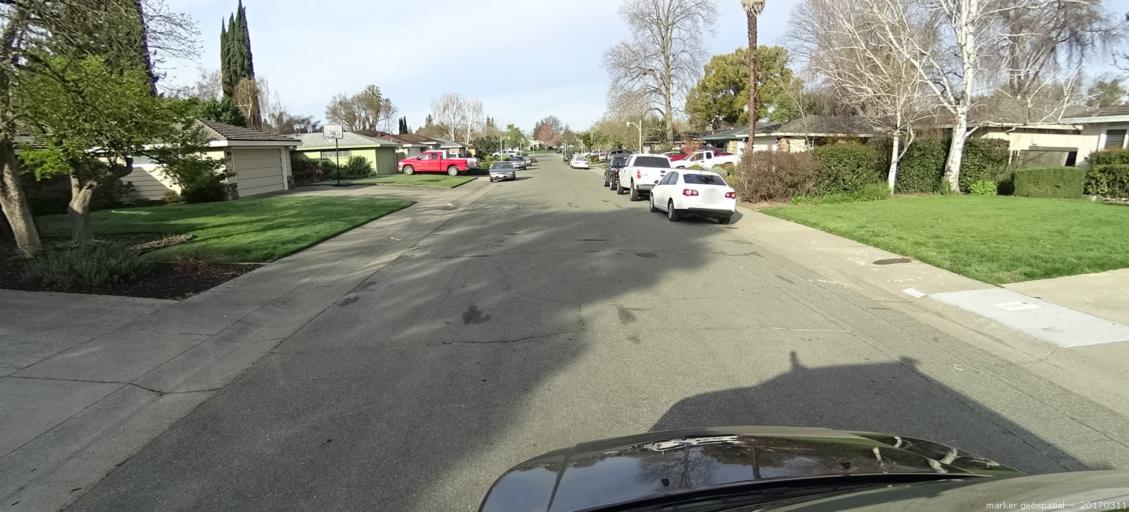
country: US
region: California
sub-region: Yolo County
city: West Sacramento
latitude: 38.5156
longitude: -121.5338
